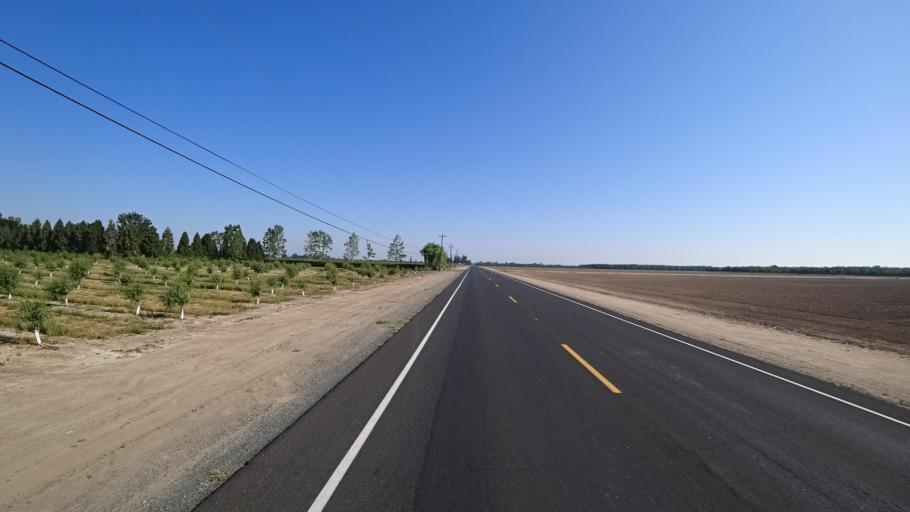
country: US
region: California
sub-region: Kings County
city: Lucerne
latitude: 36.3882
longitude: -119.6731
